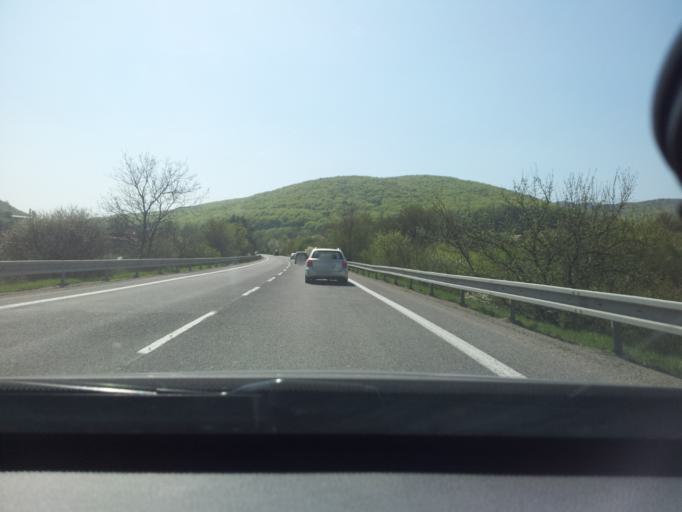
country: SK
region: Trenciansky
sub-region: Okres Trencin
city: Trencin
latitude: 48.8319
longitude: 18.0593
